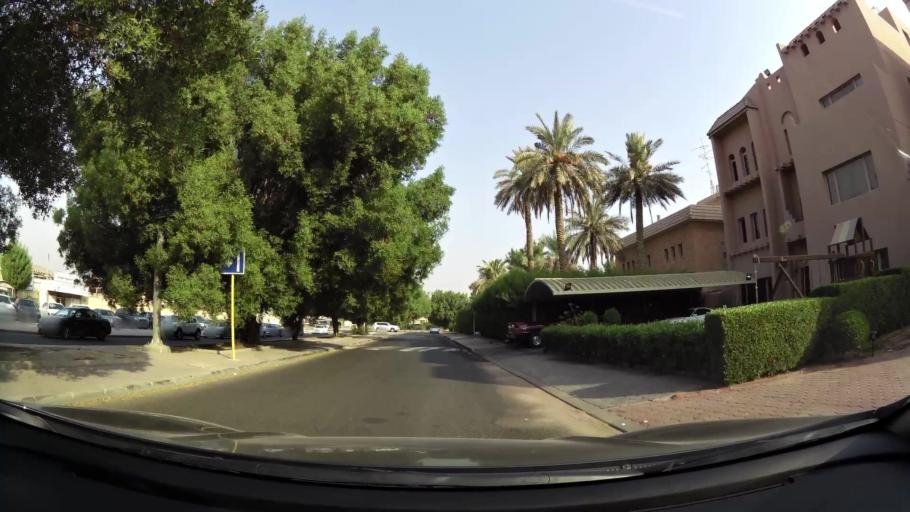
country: KW
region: Muhafazat Hawalli
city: Salwa
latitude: 29.2733
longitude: 48.0760
